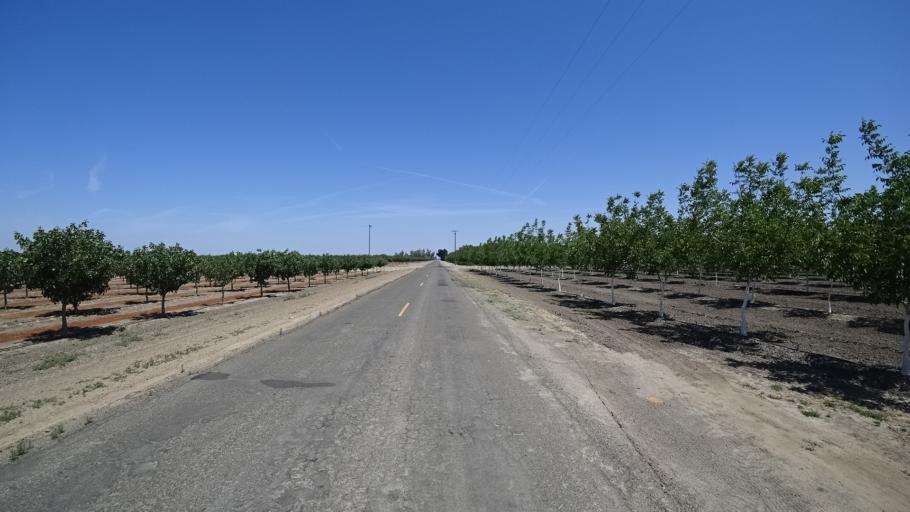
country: US
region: California
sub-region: Kings County
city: Armona
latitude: 36.2464
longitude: -119.7268
